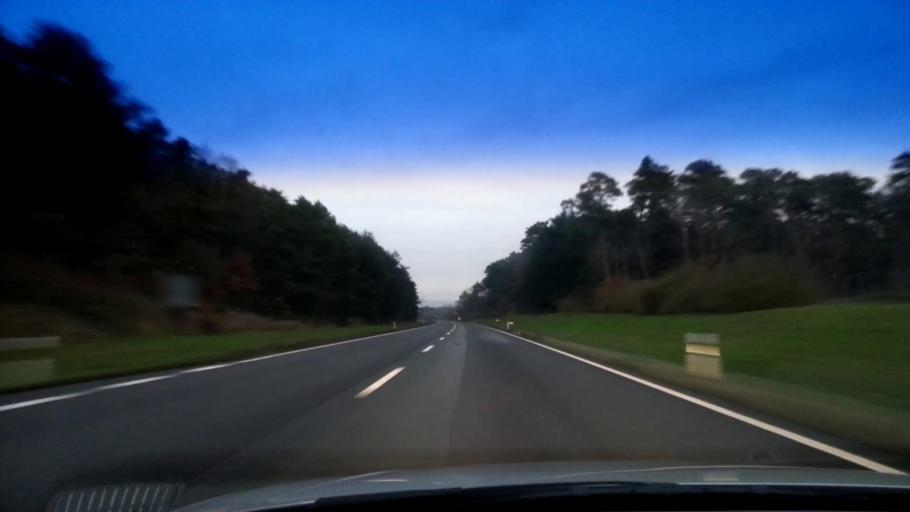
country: DE
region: Bavaria
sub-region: Upper Franconia
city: Pettstadt
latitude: 49.7800
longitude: 10.9109
